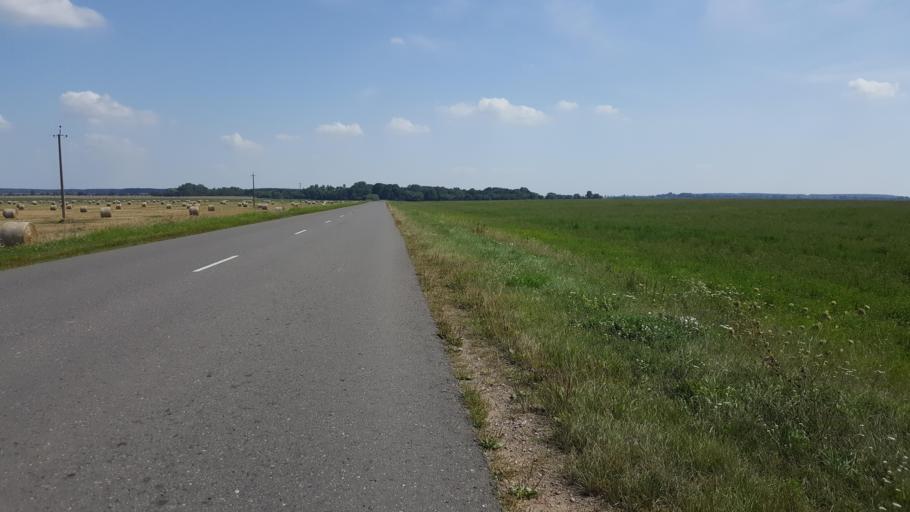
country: BY
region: Brest
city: Kamyanyuki
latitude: 52.4978
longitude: 23.6720
